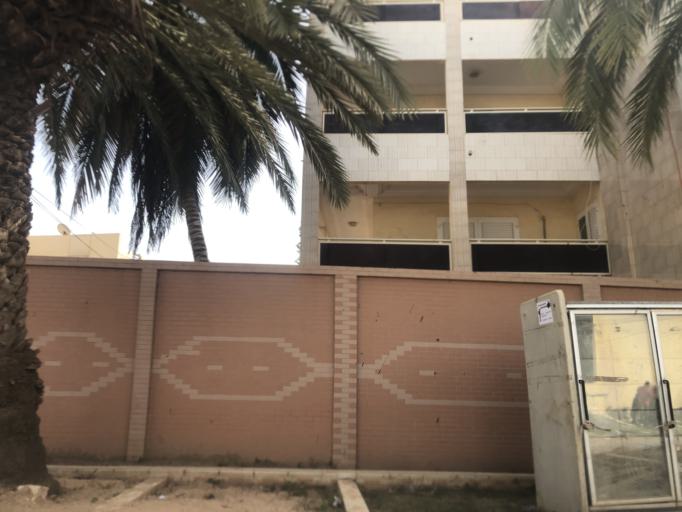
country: SN
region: Dakar
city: Mermoz Boabab
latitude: 14.7330
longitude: -17.4957
